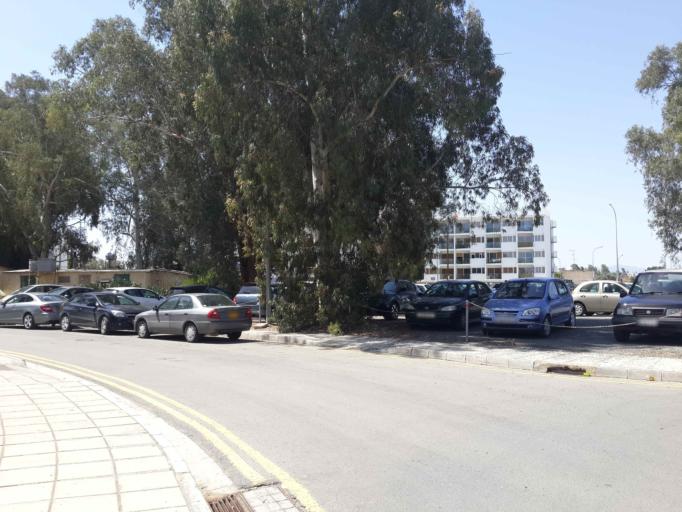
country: CY
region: Lefkosia
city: Nicosia
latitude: 35.1570
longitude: 33.3395
